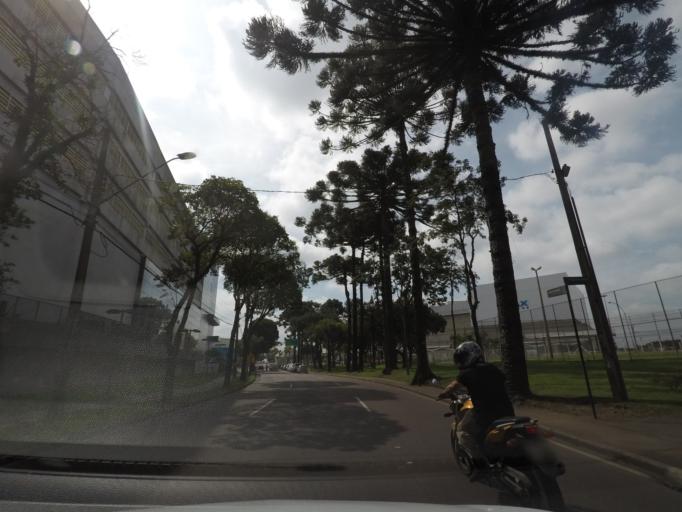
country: BR
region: Parana
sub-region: Curitiba
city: Curitiba
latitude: -25.4788
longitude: -49.2934
